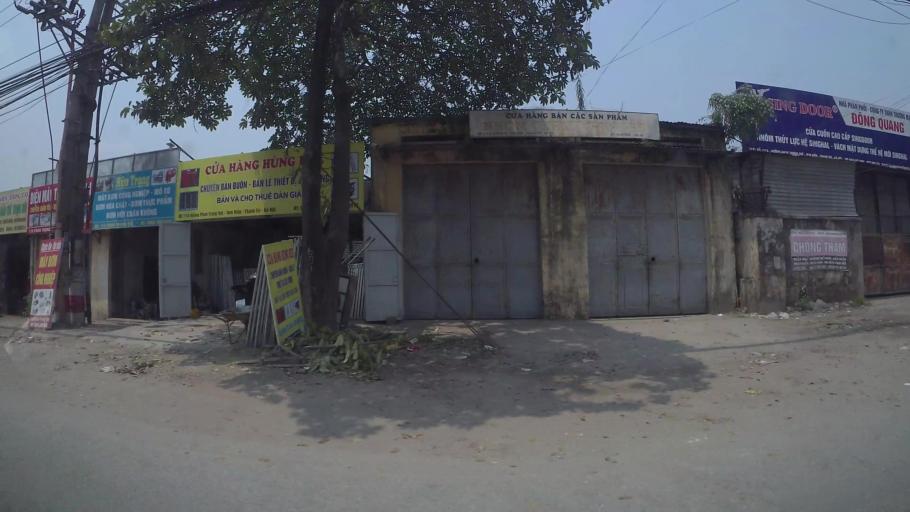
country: VN
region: Ha Noi
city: Van Dien
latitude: 20.9437
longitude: 105.8399
